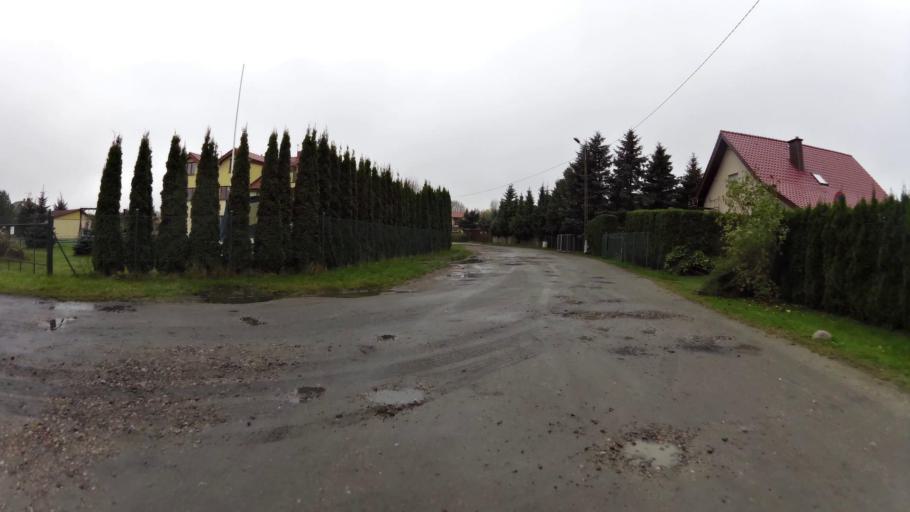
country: PL
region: West Pomeranian Voivodeship
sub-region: Powiat koszalinski
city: Mielno
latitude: 54.2566
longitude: 16.0997
